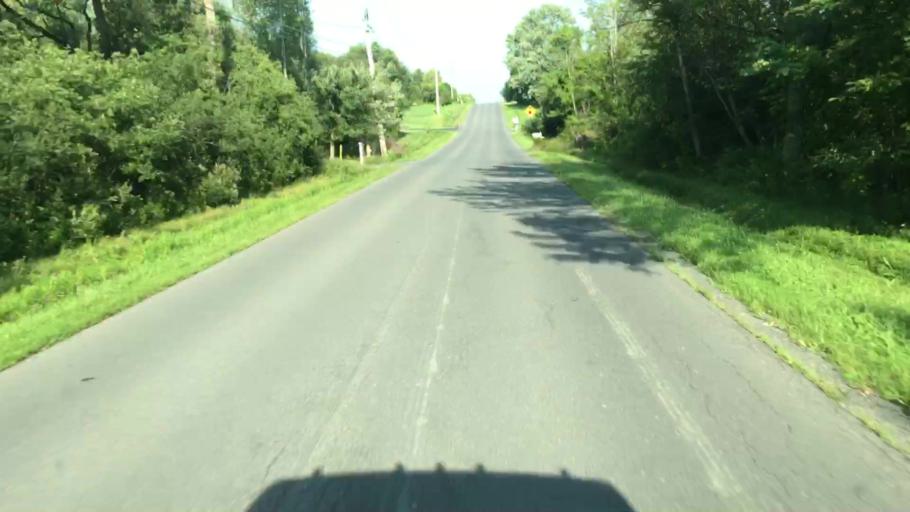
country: US
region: New York
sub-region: Onondaga County
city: Skaneateles
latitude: 42.9641
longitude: -76.4300
